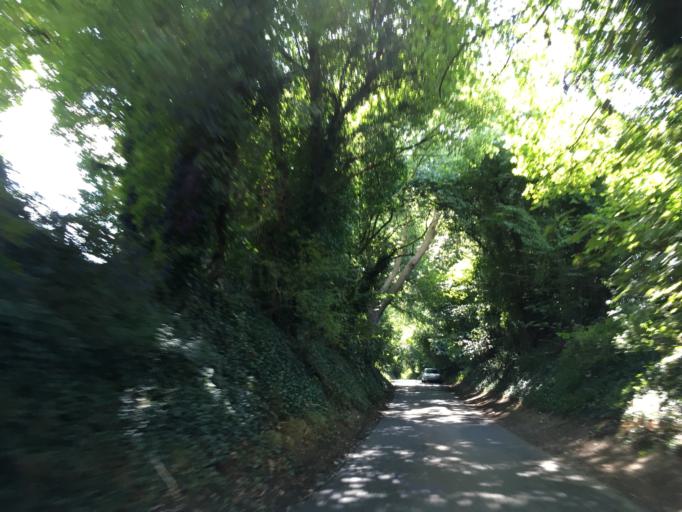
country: GB
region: England
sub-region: Hampshire
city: Colden Common
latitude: 51.0224
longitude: -1.2724
